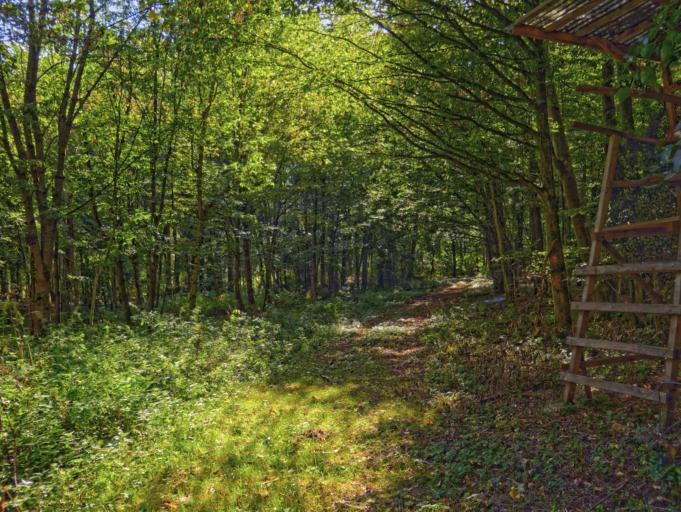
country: DE
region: Bavaria
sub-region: Regierungsbezirk Unterfranken
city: Donnersdorf
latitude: 50.0041
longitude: 10.3895
